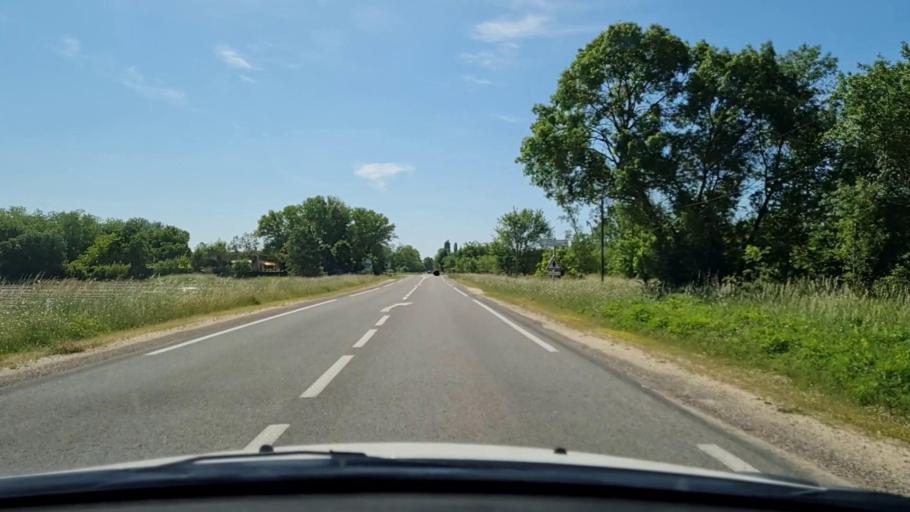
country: FR
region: Languedoc-Roussillon
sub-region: Departement du Gard
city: Saint-Genies-de-Malgoires
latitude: 43.9586
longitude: 4.2392
